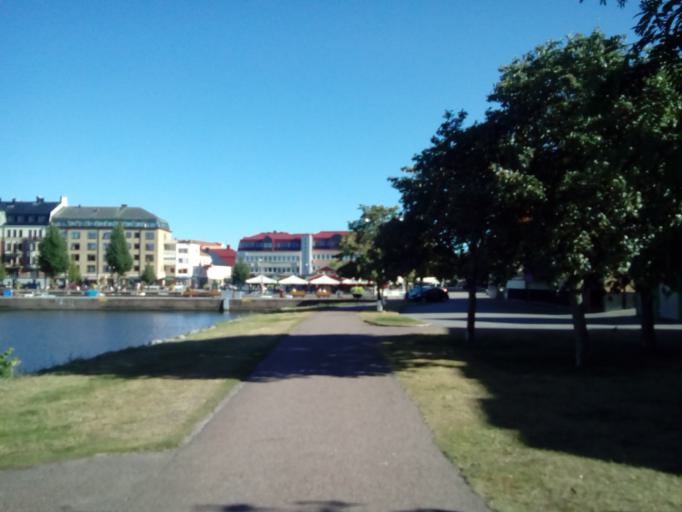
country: SE
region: Kalmar
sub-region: Vasterviks Kommun
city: Vaestervik
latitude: 57.7604
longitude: 16.6372
